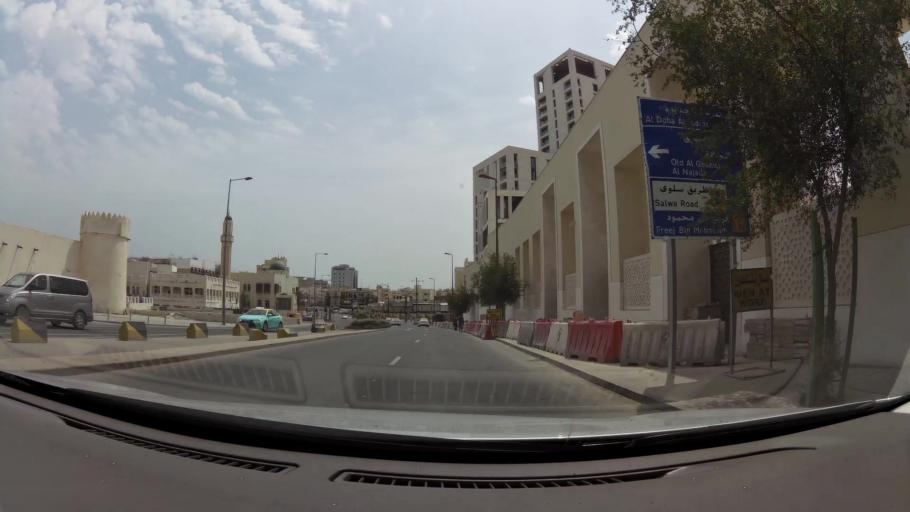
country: QA
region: Baladiyat ad Dawhah
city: Doha
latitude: 25.2866
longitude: 51.5305
